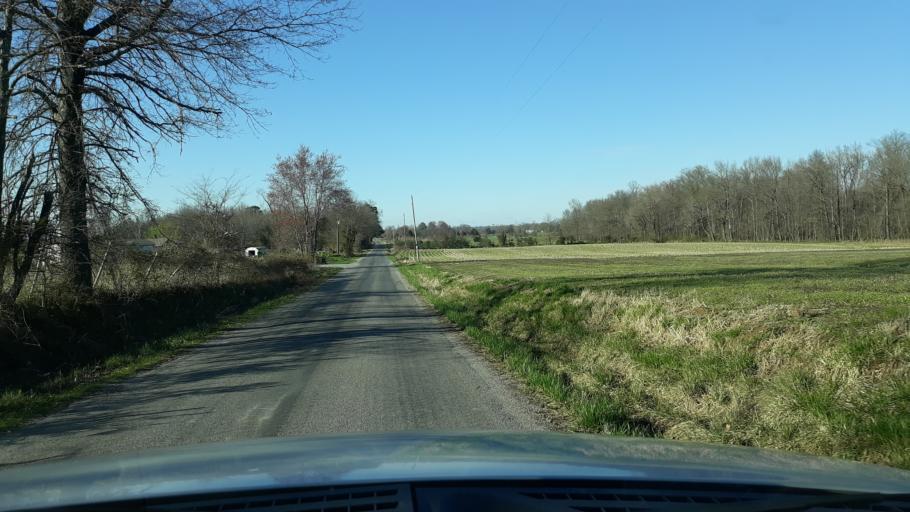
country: US
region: Illinois
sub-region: Saline County
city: Harrisburg
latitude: 37.7894
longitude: -88.6056
